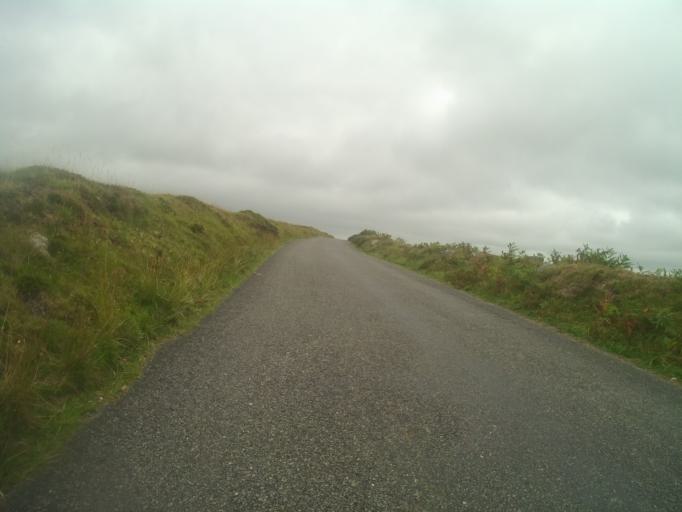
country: GB
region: England
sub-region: Devon
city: Buckfastleigh
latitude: 50.5302
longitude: -3.8765
